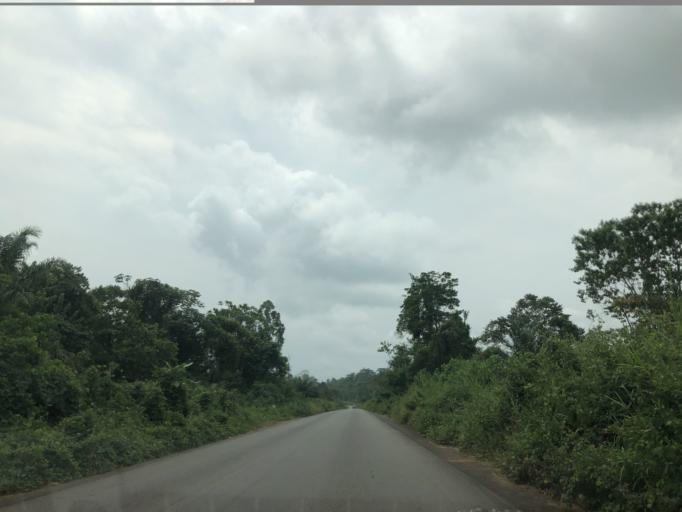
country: CM
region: Littoral
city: Edea
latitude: 3.6725
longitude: 10.1104
